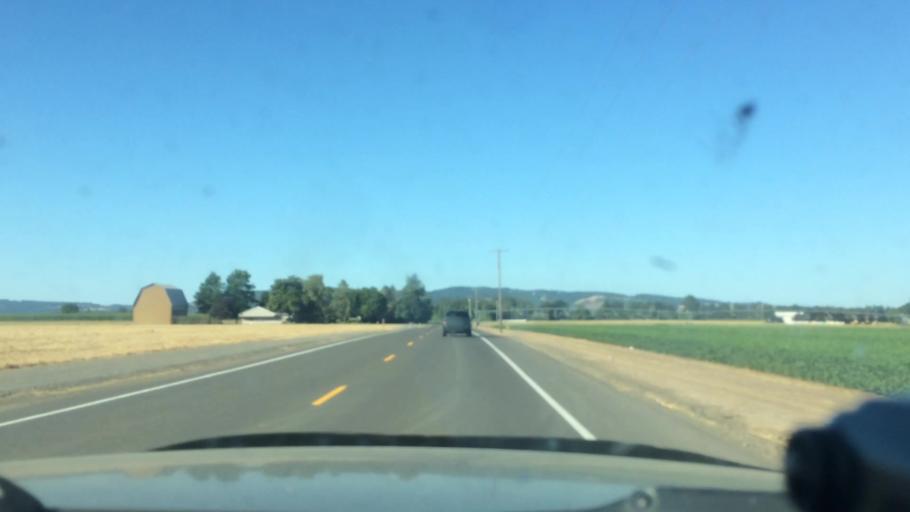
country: US
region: Oregon
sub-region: Yamhill County
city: Newberg
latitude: 45.2379
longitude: -122.9577
